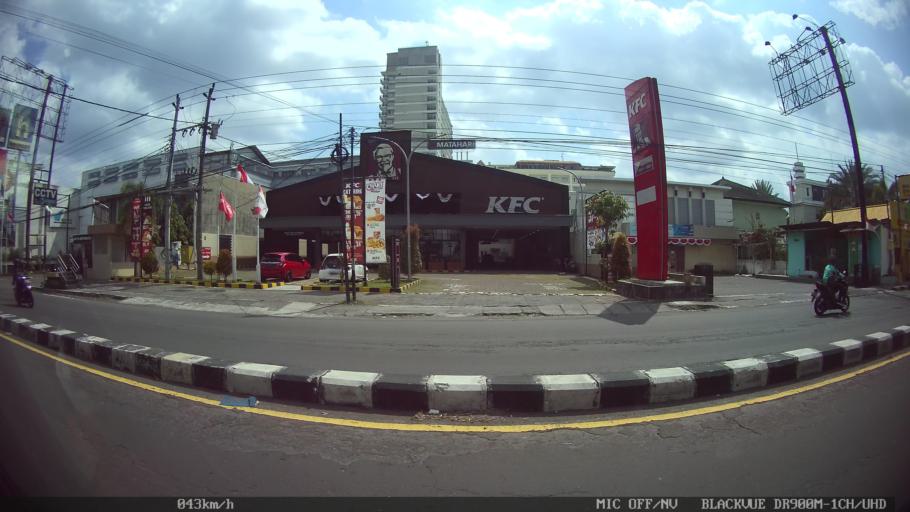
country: ID
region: Daerah Istimewa Yogyakarta
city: Melati
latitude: -7.7526
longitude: 110.3623
